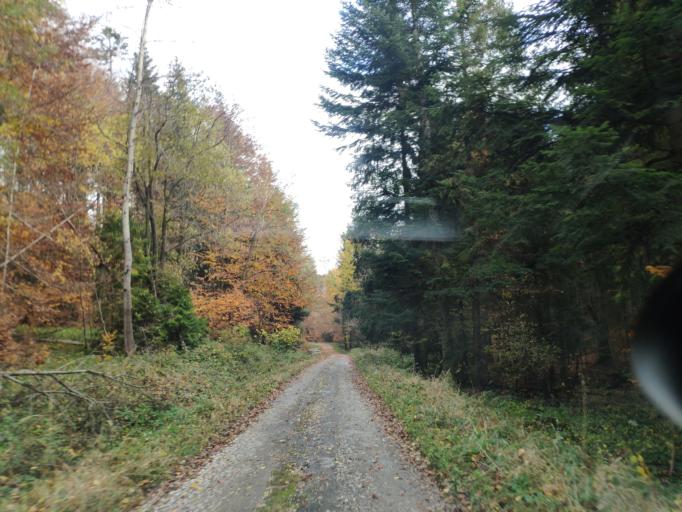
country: SK
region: Kosicky
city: Gelnica
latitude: 48.7615
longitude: 20.9755
